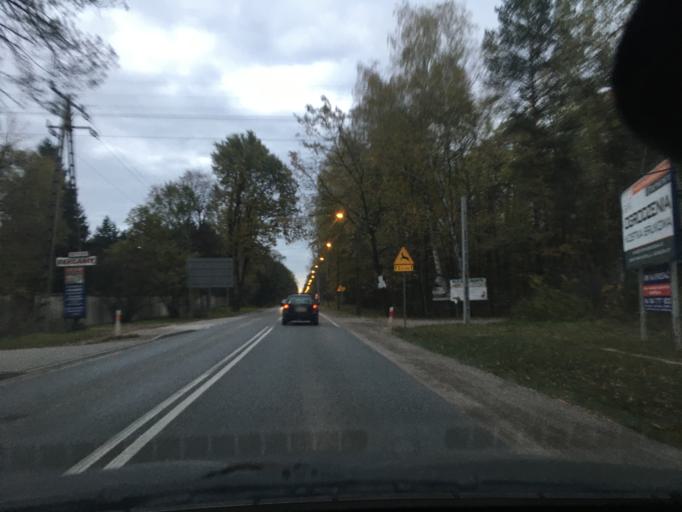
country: PL
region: Masovian Voivodeship
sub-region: Powiat piaseczynski
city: Lesznowola
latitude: 52.1007
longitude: 20.8914
